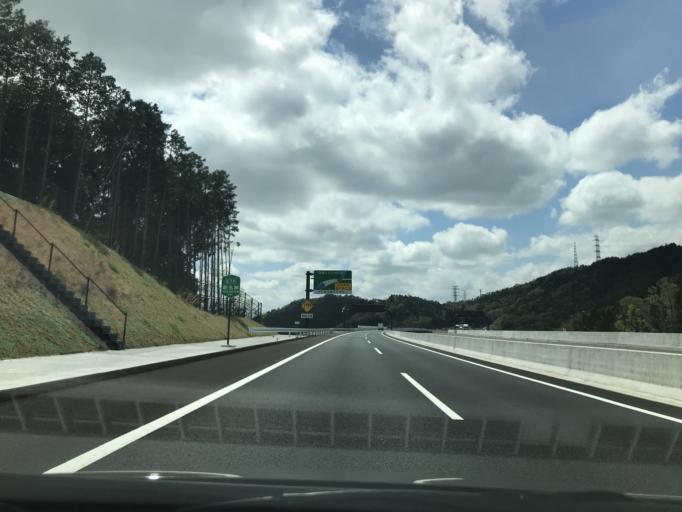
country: JP
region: Osaka
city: Mino
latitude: 34.8764
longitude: 135.5252
